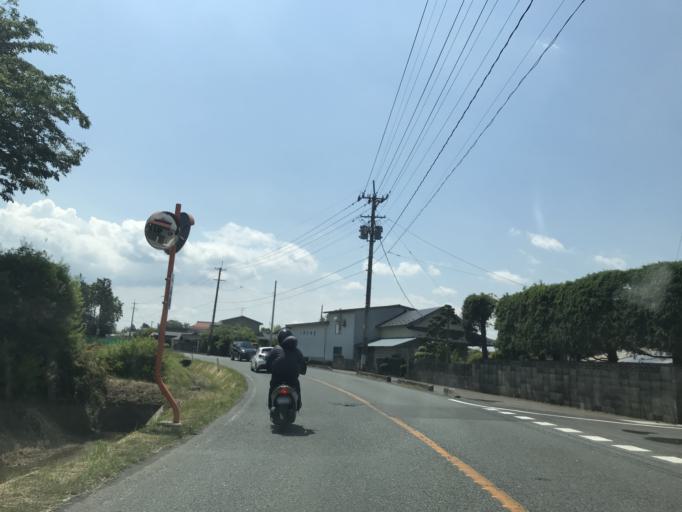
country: JP
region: Miyagi
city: Kogota
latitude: 38.5765
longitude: 141.0334
